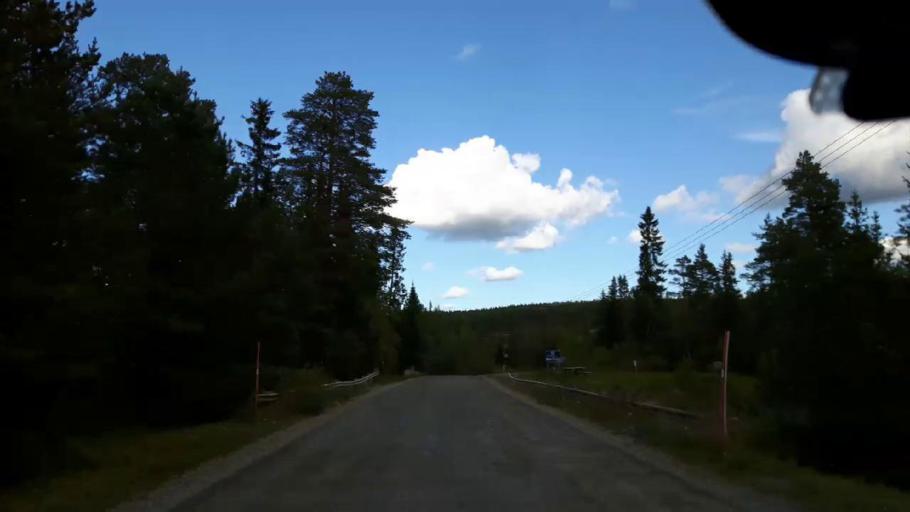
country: SE
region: Jaemtland
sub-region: Stroemsunds Kommun
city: Stroemsund
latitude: 63.4253
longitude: 15.8056
